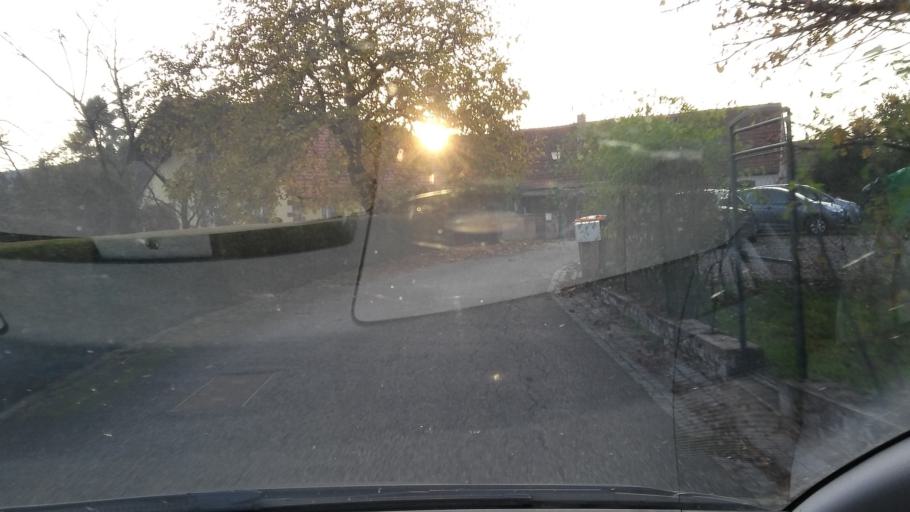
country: FR
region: Alsace
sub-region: Departement du Bas-Rhin
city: Neuwiller-les-Saverne
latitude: 48.8620
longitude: 7.3206
